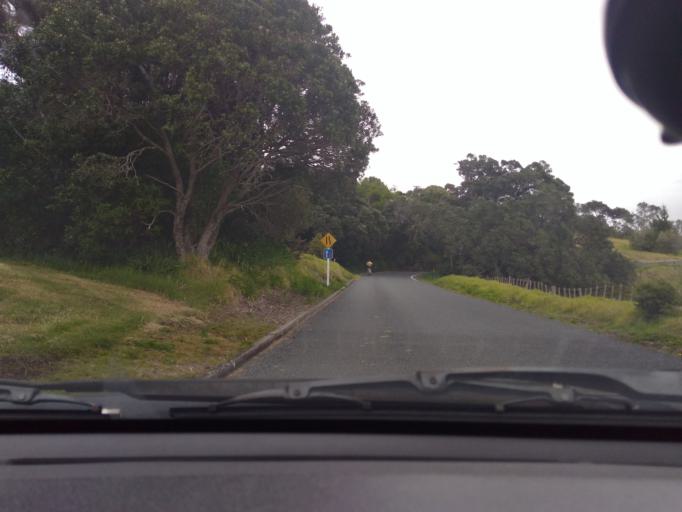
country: NZ
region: Auckland
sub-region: Auckland
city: Warkworth
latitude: -36.4507
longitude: 174.7616
